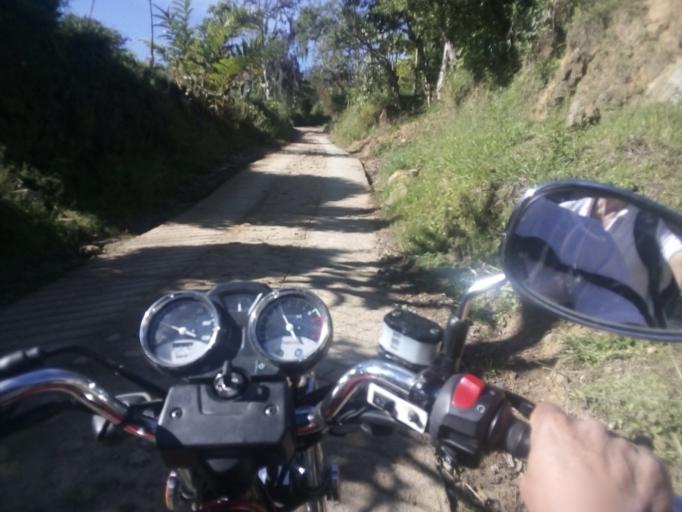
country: CO
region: Santander
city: Guepsa
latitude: 6.0045
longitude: -73.5530
